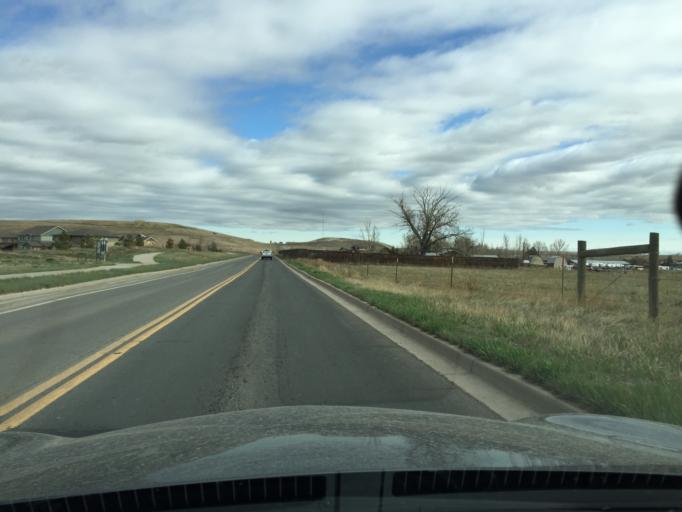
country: US
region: Colorado
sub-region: Boulder County
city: Erie
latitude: 40.0085
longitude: -105.0086
